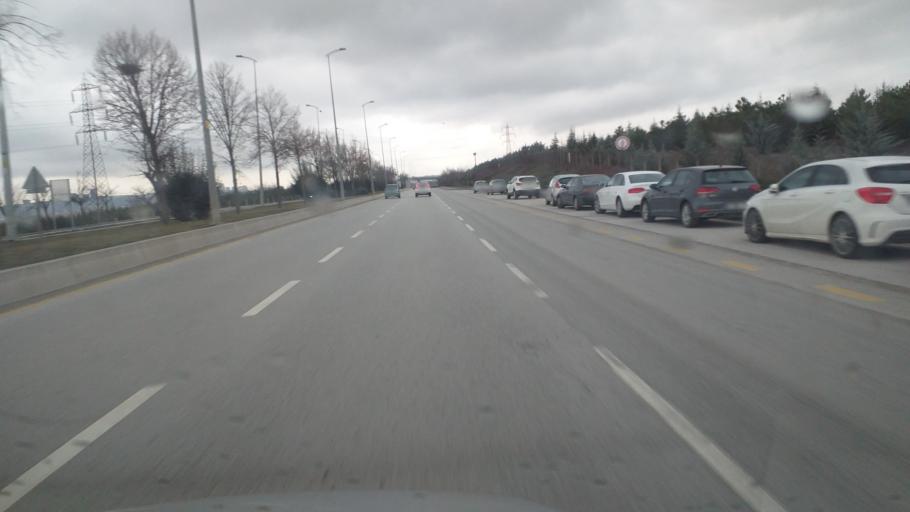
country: TR
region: Ankara
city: Batikent
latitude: 39.9028
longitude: 32.7329
